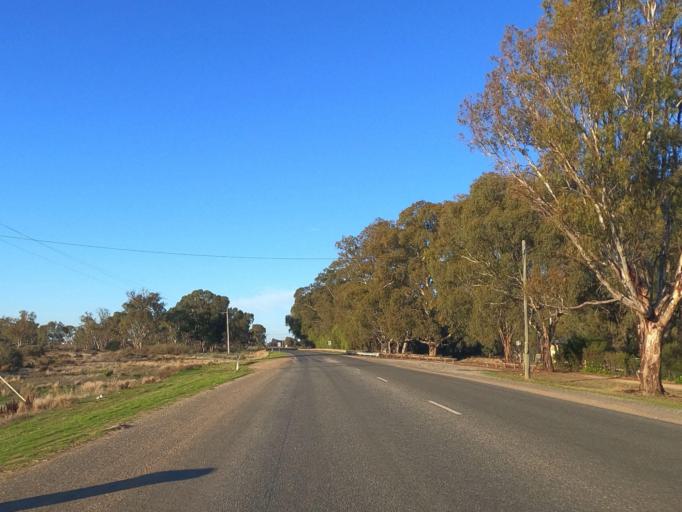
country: AU
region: Victoria
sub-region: Swan Hill
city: Swan Hill
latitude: -35.3368
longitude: 143.5706
